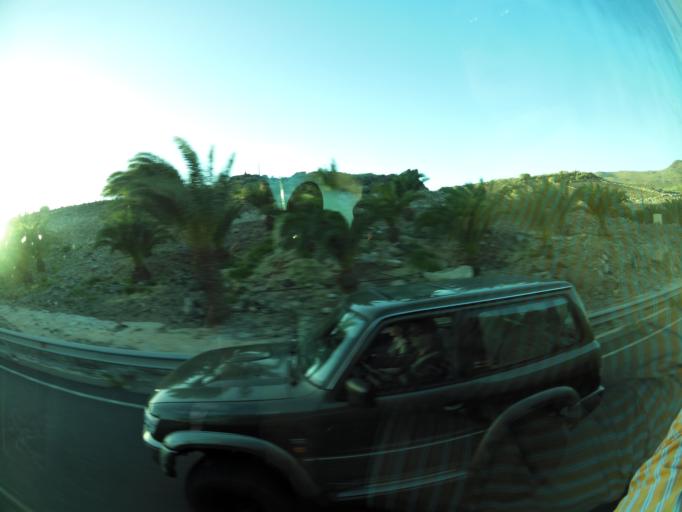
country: ES
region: Canary Islands
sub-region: Provincia de Las Palmas
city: Playa del Ingles
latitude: 27.7760
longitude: -15.5306
